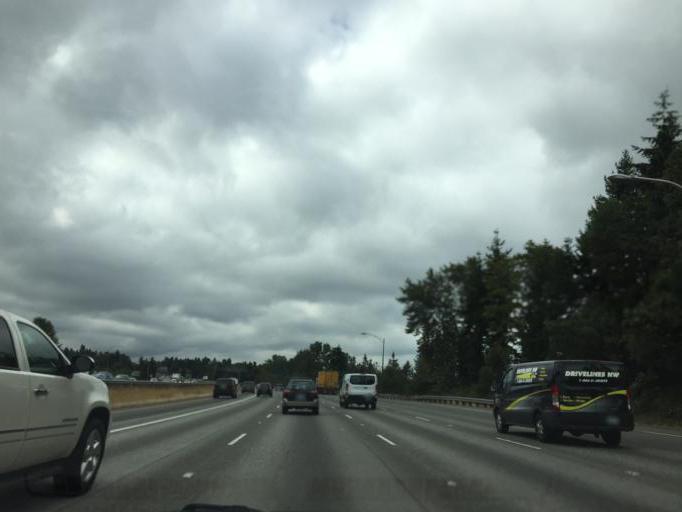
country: US
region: Washington
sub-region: King County
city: SeaTac
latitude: 47.4196
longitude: -122.2880
